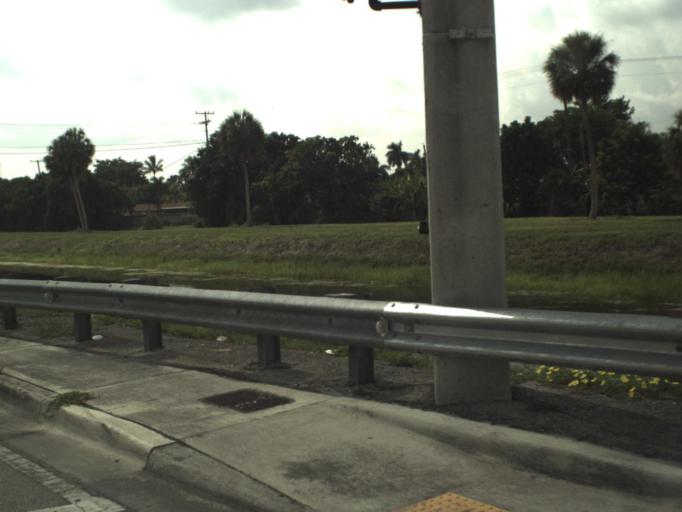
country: US
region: Florida
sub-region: Broward County
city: Plantation
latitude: 26.1357
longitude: -80.2244
